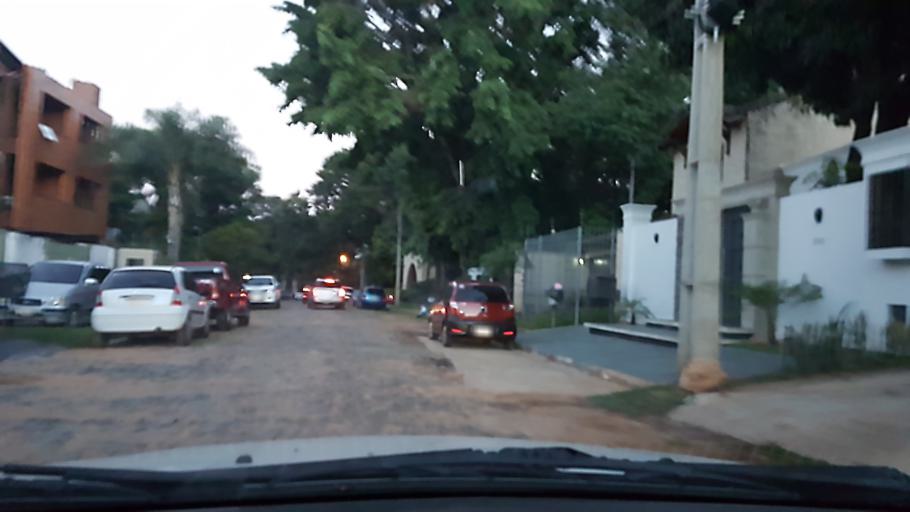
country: PY
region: Central
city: Fernando de la Mora
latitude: -25.3095
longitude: -57.5619
